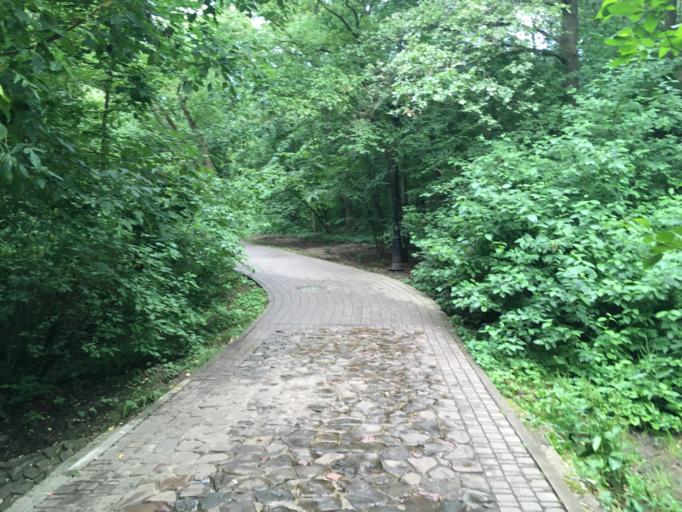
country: RU
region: Moscow
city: Ostankinskiy
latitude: 55.8309
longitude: 37.6054
